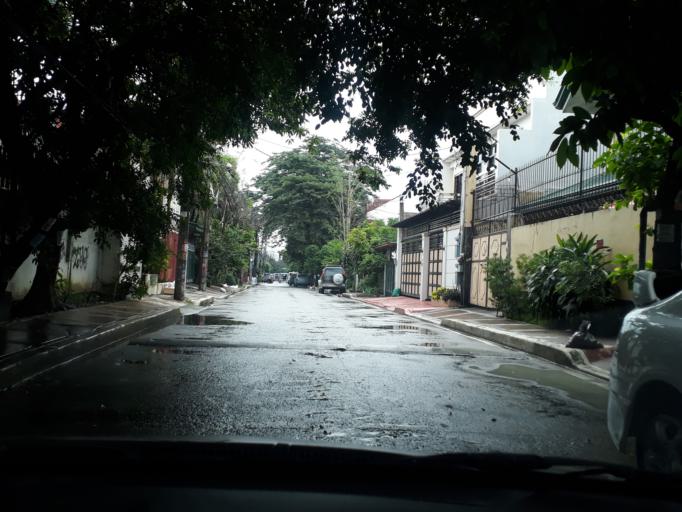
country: PH
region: Calabarzon
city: Del Monte
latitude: 14.6272
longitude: 121.0368
